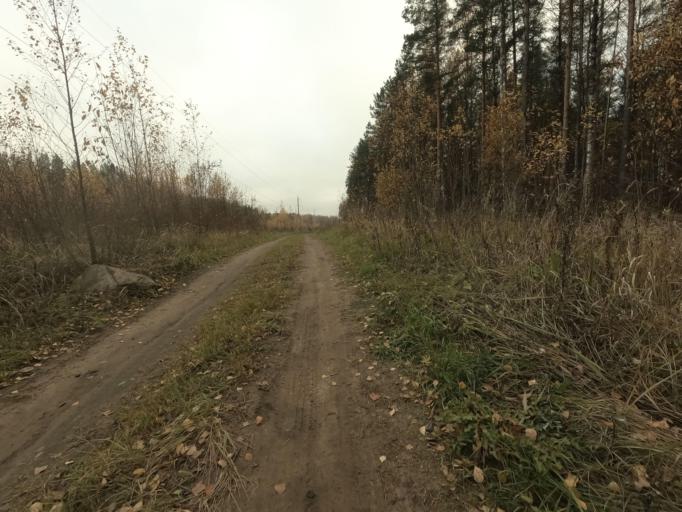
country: RU
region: Leningrad
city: Kirovsk
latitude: 59.8514
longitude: 30.9838
